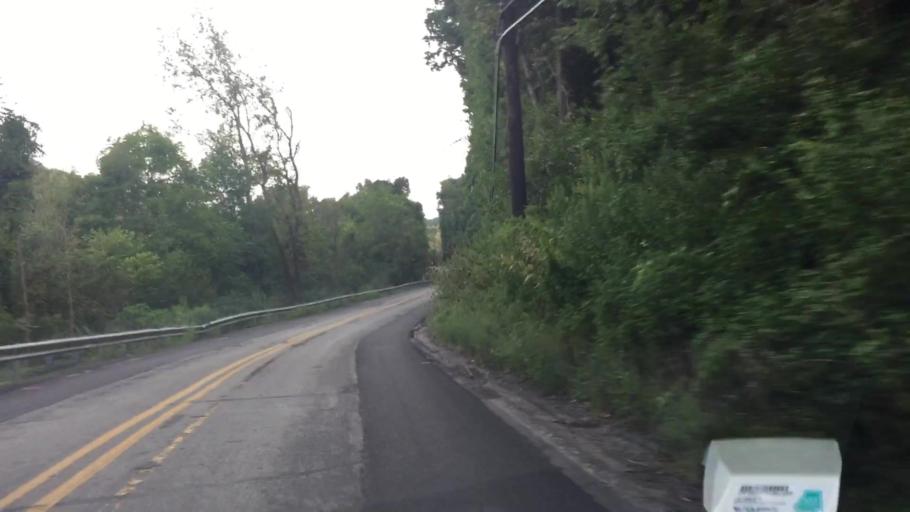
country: US
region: Pennsylvania
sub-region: Allegheny County
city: Franklin Park
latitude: 40.5564
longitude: -80.0581
